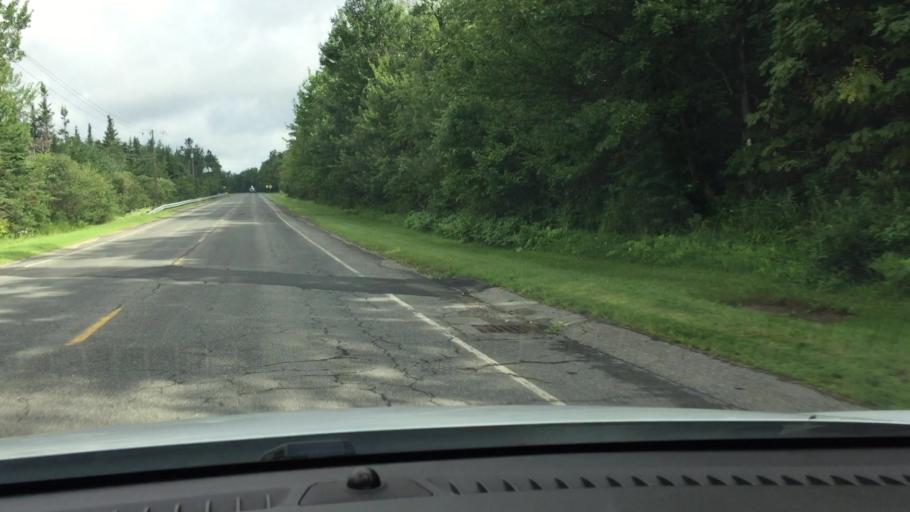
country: US
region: Massachusetts
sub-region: Berkshire County
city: Hinsdale
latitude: 42.4417
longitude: -73.0512
